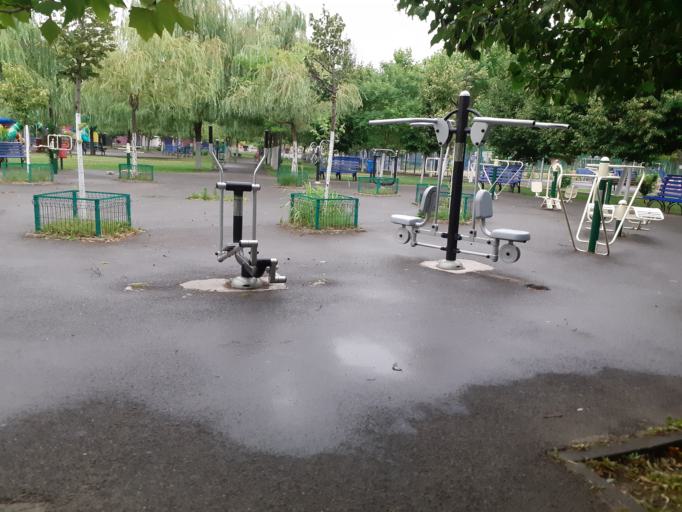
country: RO
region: Bucuresti
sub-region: Municipiul Bucuresti
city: Bucharest
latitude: 44.4036
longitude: 26.1133
